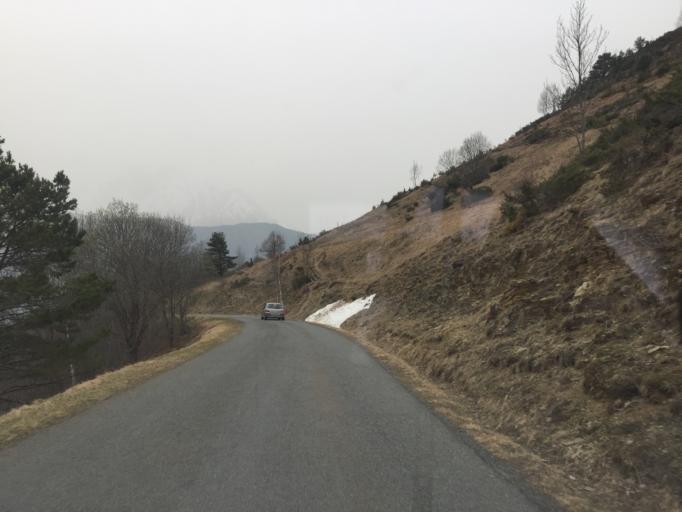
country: FR
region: Midi-Pyrenees
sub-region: Departement des Hautes-Pyrenees
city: Saint-Lary-Soulan
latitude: 42.8148
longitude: 0.3551
